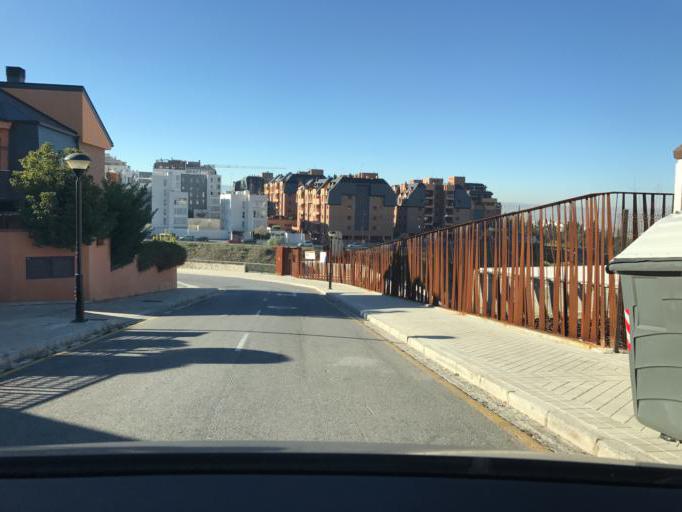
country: ES
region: Andalusia
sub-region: Provincia de Granada
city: Huetor Vega
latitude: 37.1604
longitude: -3.5757
